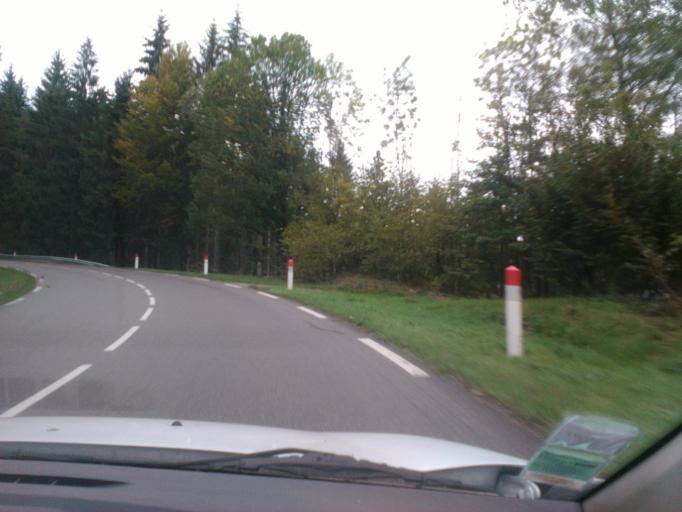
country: FR
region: Lorraine
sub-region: Departement des Vosges
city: Etival-Clairefontaine
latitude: 48.3265
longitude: 6.7878
